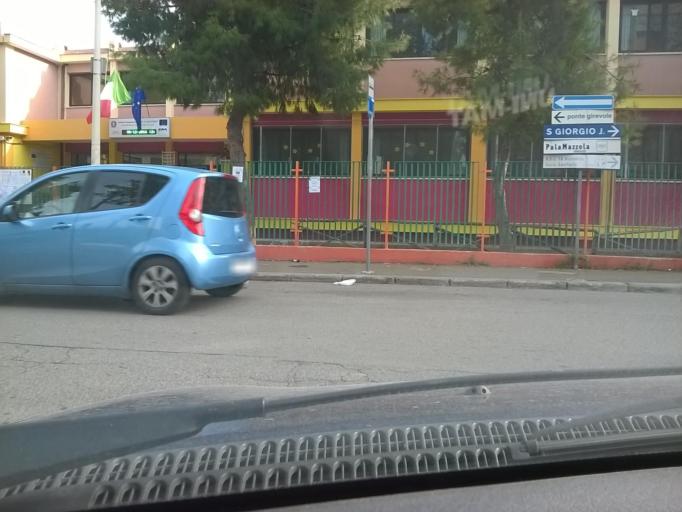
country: IT
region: Apulia
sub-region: Provincia di Taranto
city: Taranto
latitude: 40.4671
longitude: 17.2672
